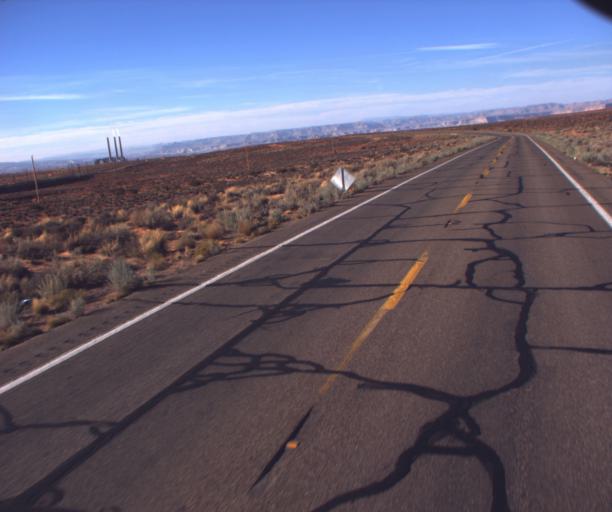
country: US
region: Arizona
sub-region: Coconino County
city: LeChee
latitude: 36.8746
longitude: -111.3429
